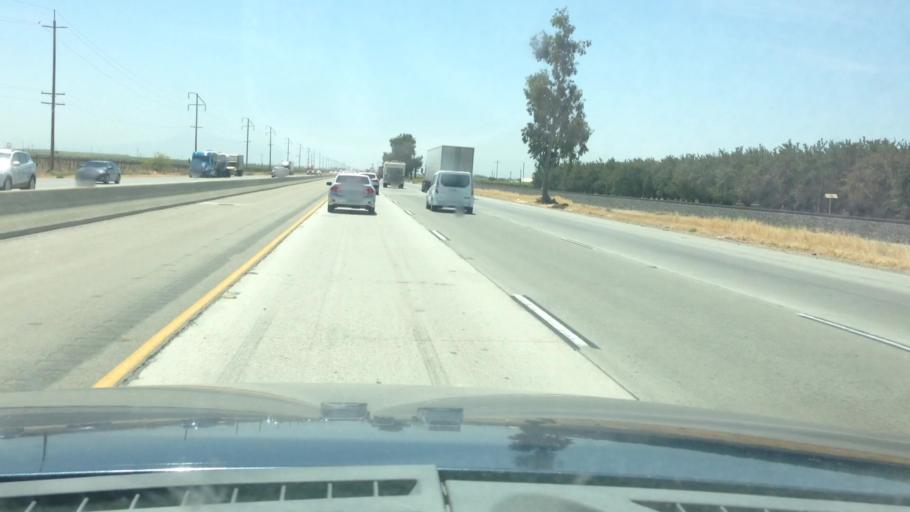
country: US
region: California
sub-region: Kern County
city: Rosedale
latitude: 35.4764
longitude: -119.1338
